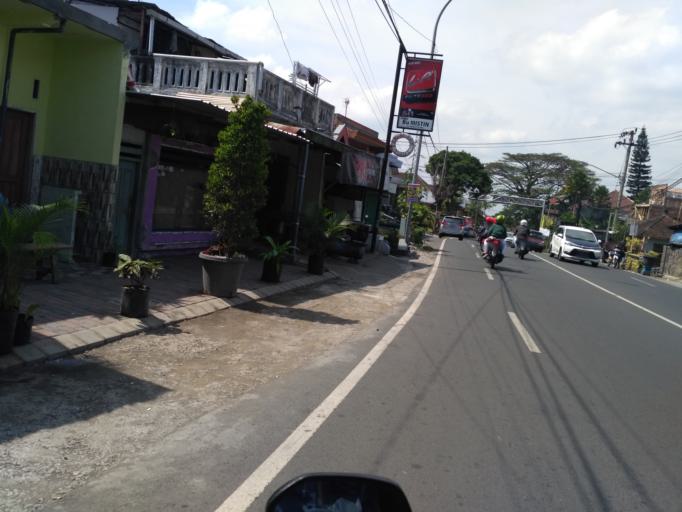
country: ID
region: East Java
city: Batu
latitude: -7.9051
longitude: 112.5738
